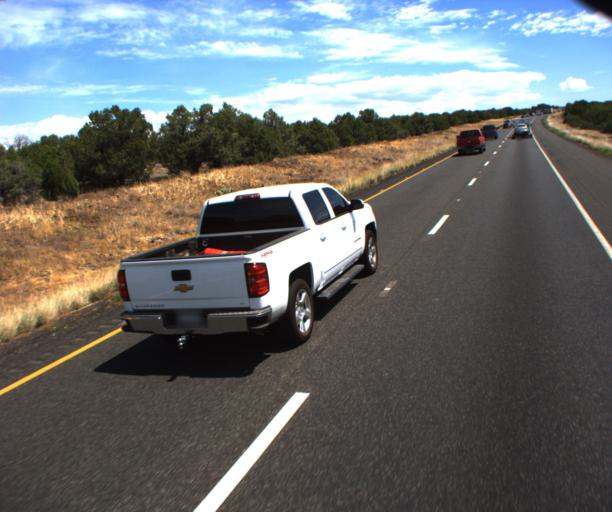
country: US
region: Arizona
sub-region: Yavapai County
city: Big Park
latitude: 34.7367
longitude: -111.6953
